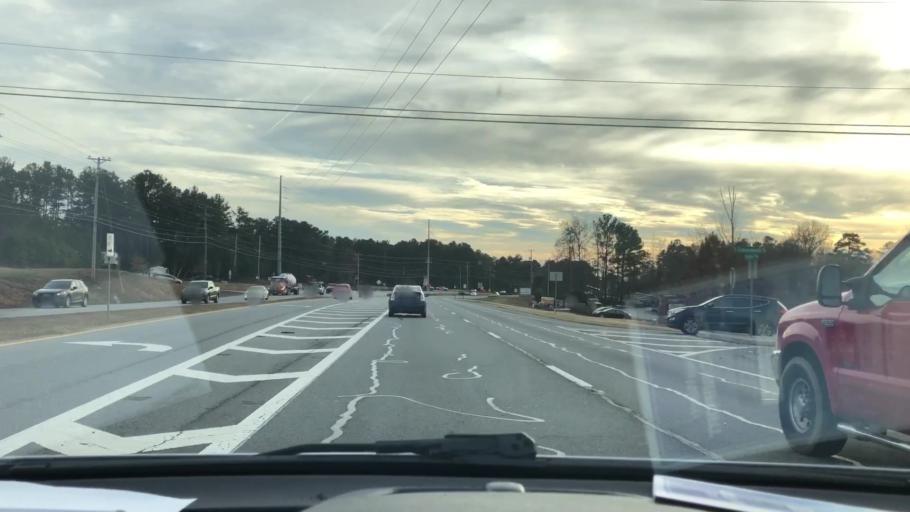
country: US
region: Georgia
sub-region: Forsyth County
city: Cumming
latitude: 34.1225
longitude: -84.1717
